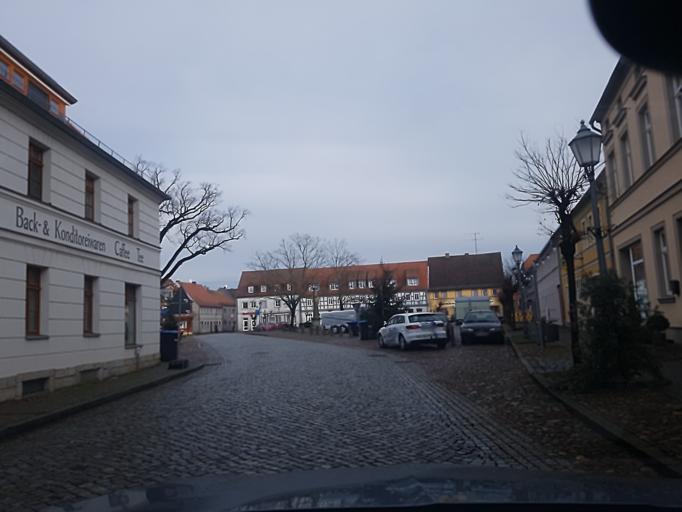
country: DE
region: Brandenburg
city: Falkenberg
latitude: 51.5944
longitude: 13.2998
